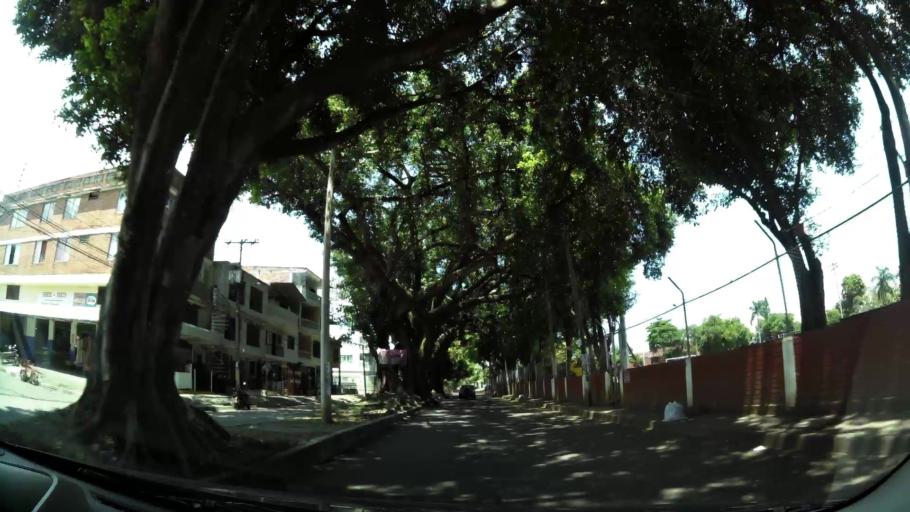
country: CO
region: Valle del Cauca
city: Cali
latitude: 3.4485
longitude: -76.4962
